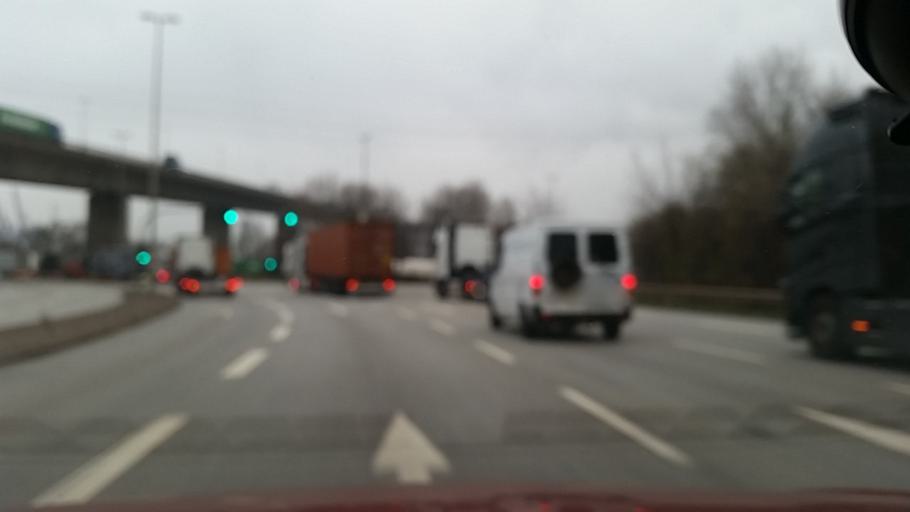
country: DE
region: Hamburg
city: Altona
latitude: 53.5177
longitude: 9.9273
